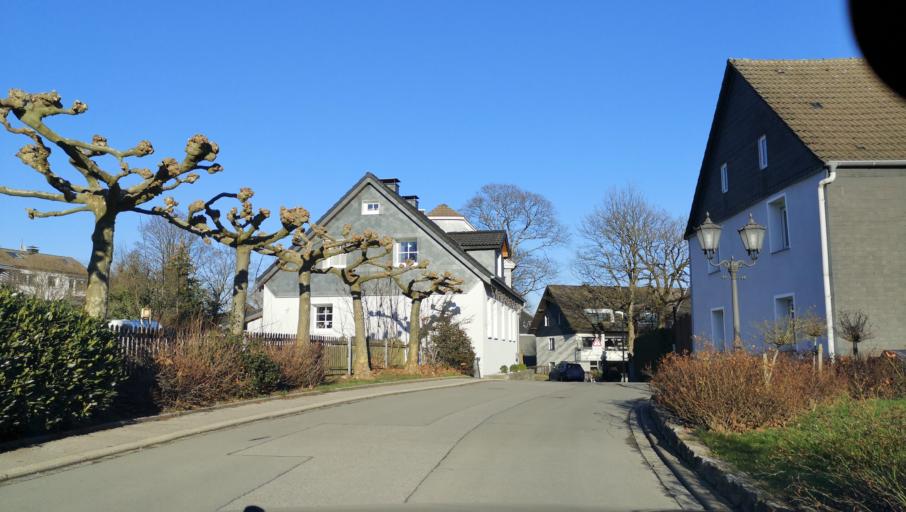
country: DE
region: North Rhine-Westphalia
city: Ennepetal
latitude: 51.2672
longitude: 7.3846
